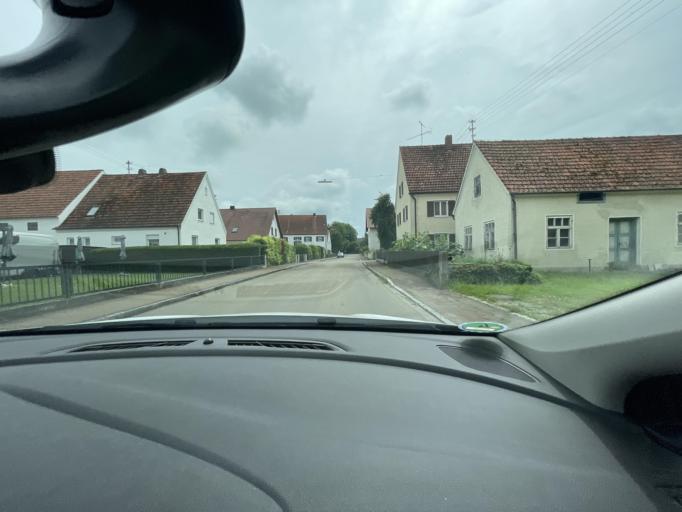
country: DE
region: Bavaria
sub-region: Swabia
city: Ellgau
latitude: 48.5976
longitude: 10.8675
